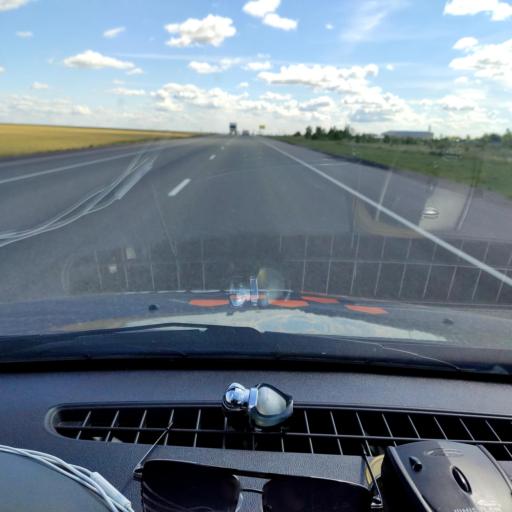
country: RU
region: Lipetsk
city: Borinskoye
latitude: 52.4720
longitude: 39.3611
